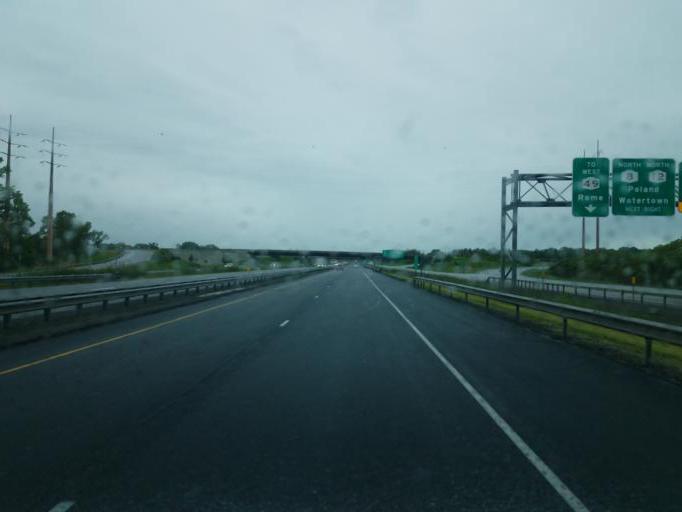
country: US
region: New York
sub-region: Oneida County
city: Utica
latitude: 43.1199
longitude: -75.2245
